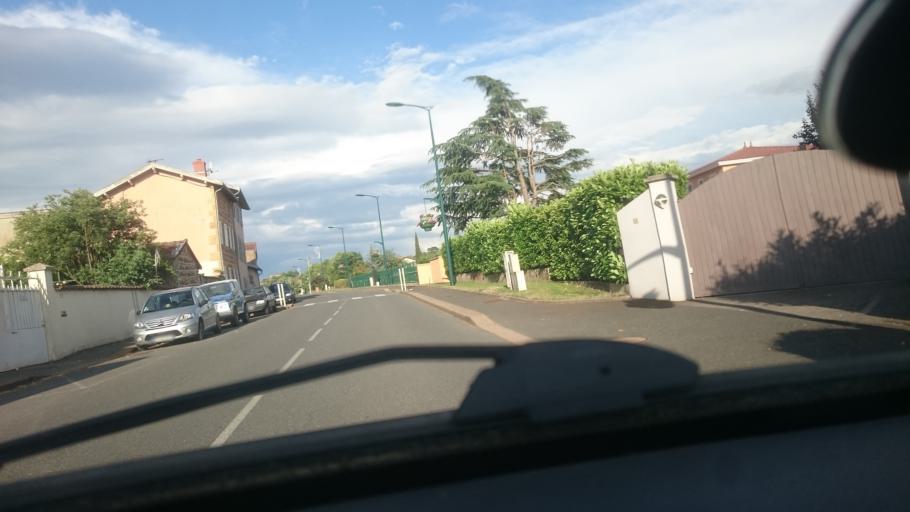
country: FR
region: Rhone-Alpes
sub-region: Departement du Rhone
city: Saint-Romain-de-Popey
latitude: 45.8787
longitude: 4.5518
